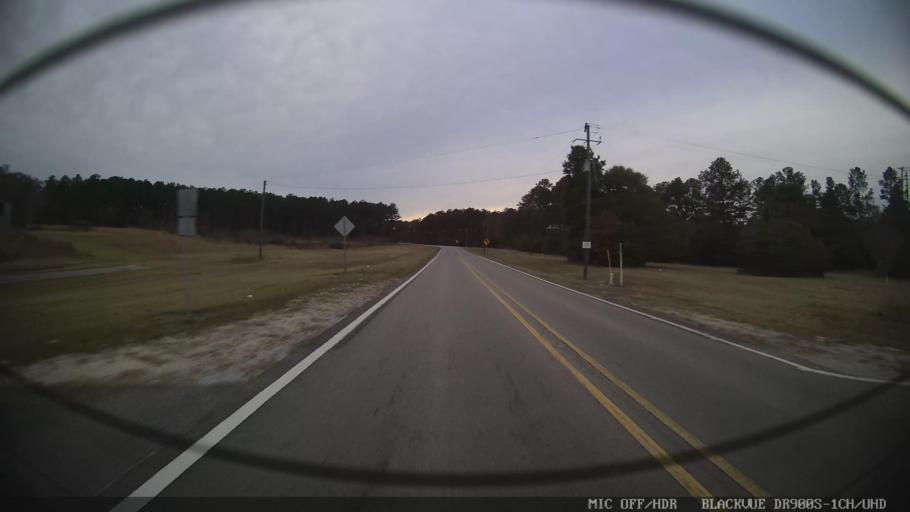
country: US
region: Mississippi
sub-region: Clarke County
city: Quitman
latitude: 32.0427
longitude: -88.7470
